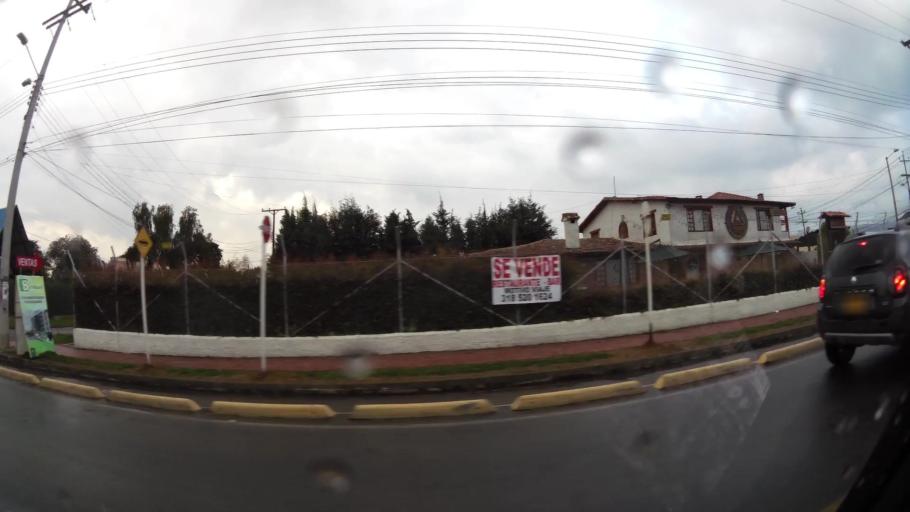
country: CO
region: Cundinamarca
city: Chia
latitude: 4.8684
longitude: -74.0548
